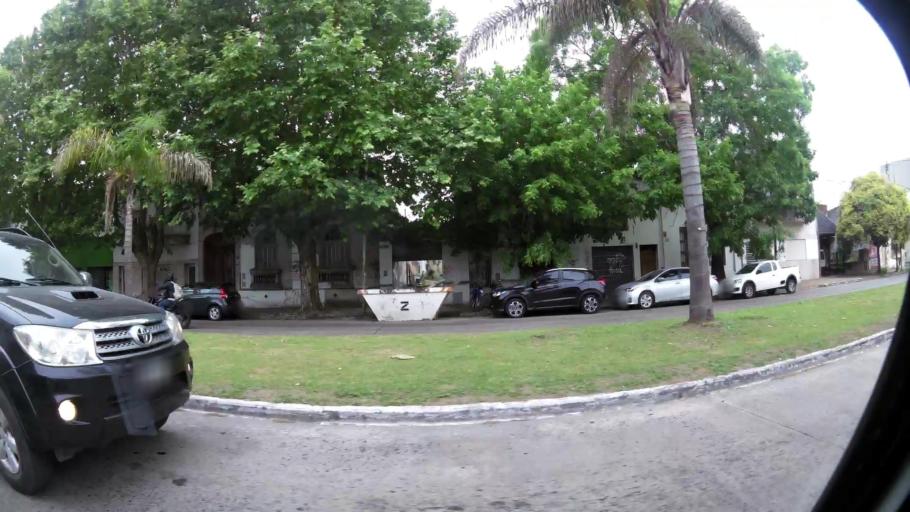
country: AR
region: Buenos Aires
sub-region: Partido de La Plata
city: La Plata
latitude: -34.9349
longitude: -57.9538
